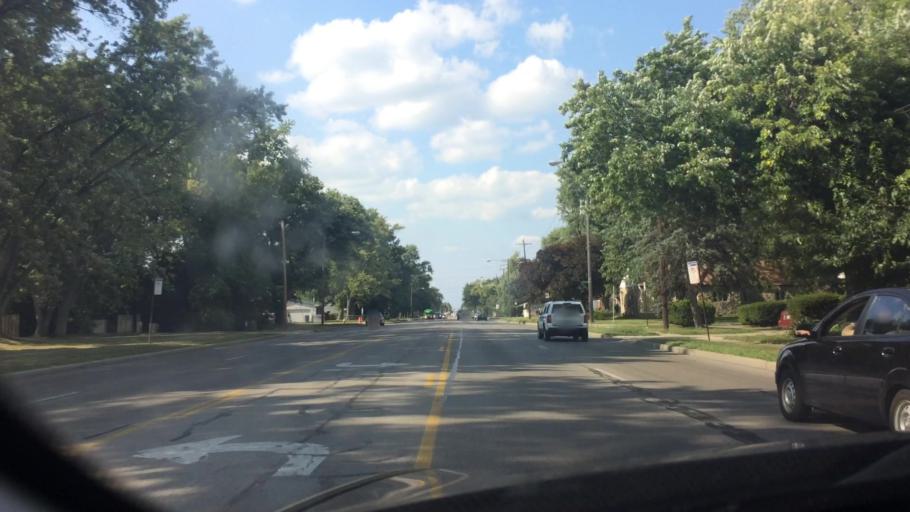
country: US
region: Ohio
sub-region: Wood County
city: Perrysburg
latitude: 41.6042
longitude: -83.6257
